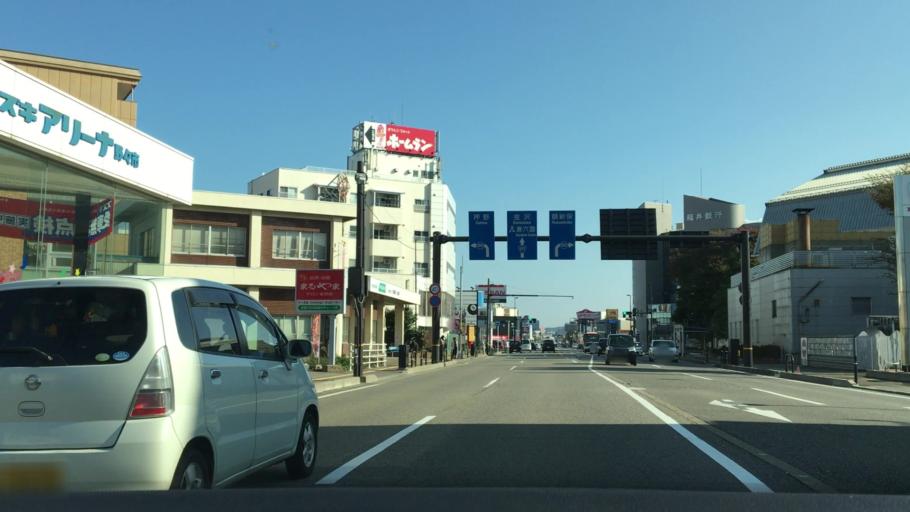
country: JP
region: Ishikawa
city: Nonoichi
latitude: 36.5353
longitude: 136.6157
